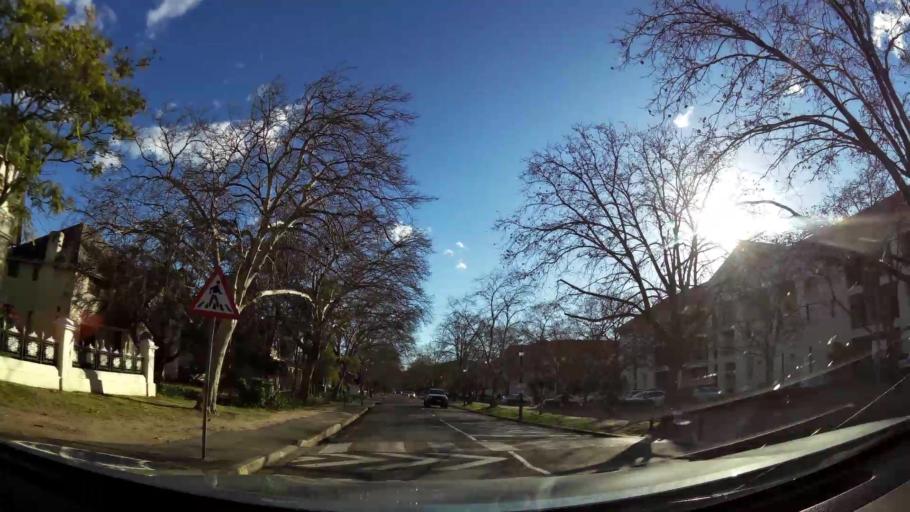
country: ZA
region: Western Cape
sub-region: Cape Winelands District Municipality
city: Stellenbosch
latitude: -33.9337
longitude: 18.8678
